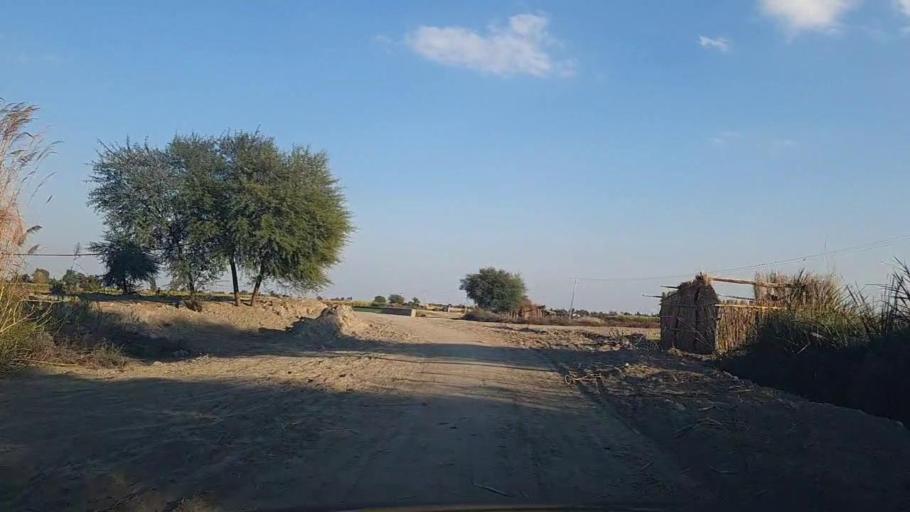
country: PK
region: Sindh
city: Jhol
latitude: 25.9196
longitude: 69.0406
